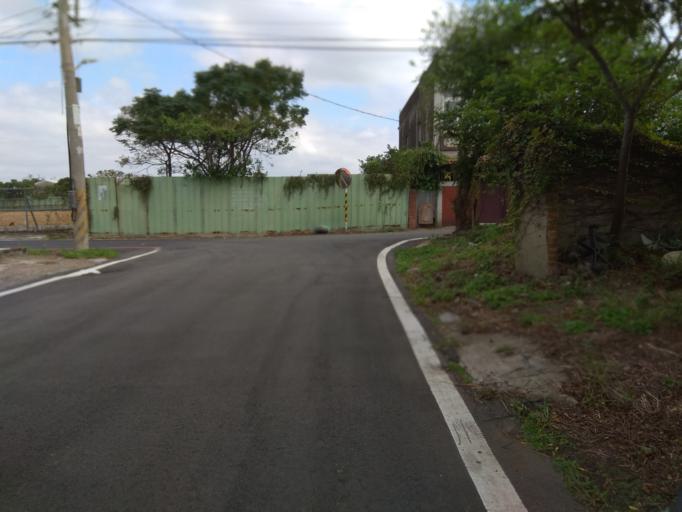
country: TW
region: Taiwan
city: Taoyuan City
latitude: 25.0602
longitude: 121.2316
